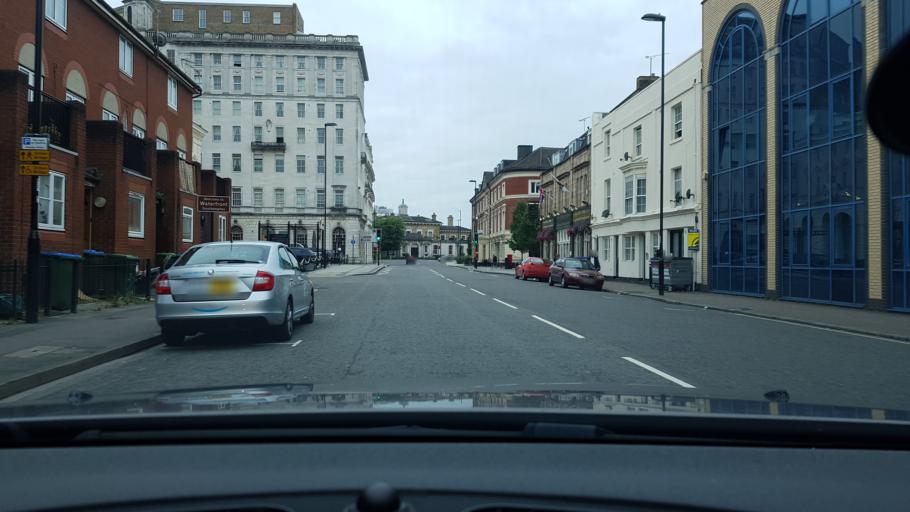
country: GB
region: England
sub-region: Southampton
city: Southampton
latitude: 50.8985
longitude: -1.3966
